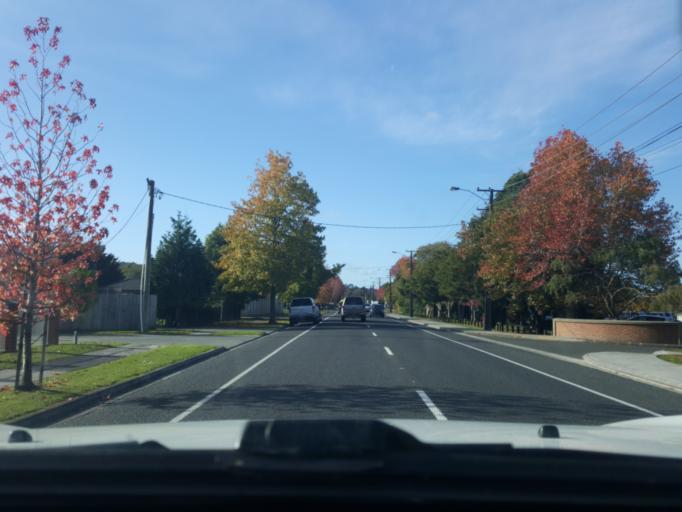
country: NZ
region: Auckland
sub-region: Auckland
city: Rosebank
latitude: -36.7612
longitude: 174.5887
